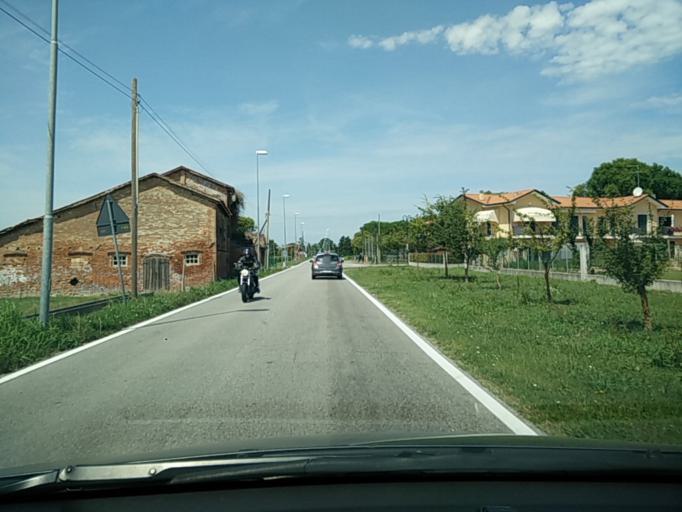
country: IT
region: Veneto
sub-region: Provincia di Venezia
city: Passarella
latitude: 45.5698
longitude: 12.6240
